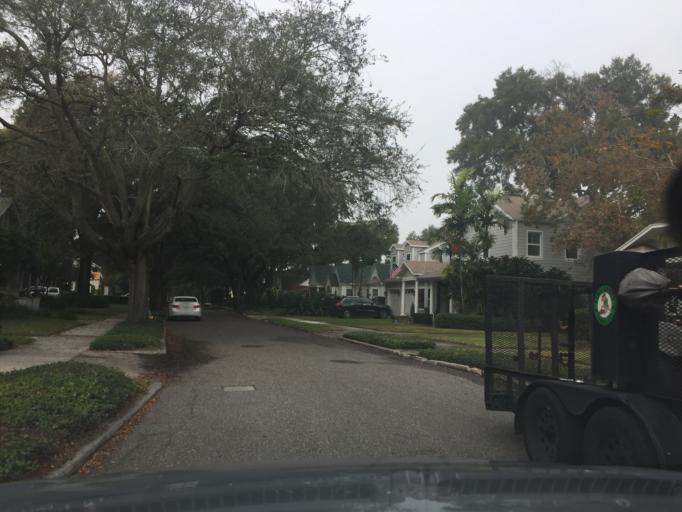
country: US
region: Florida
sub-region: Hillsborough County
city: Tampa
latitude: 27.9324
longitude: -82.4861
